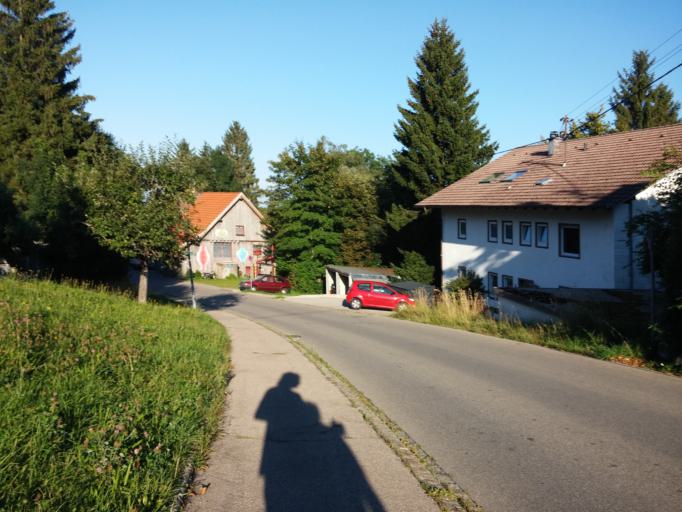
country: DE
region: Bavaria
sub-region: Swabia
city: Wiggensbach
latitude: 47.7439
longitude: 10.2203
